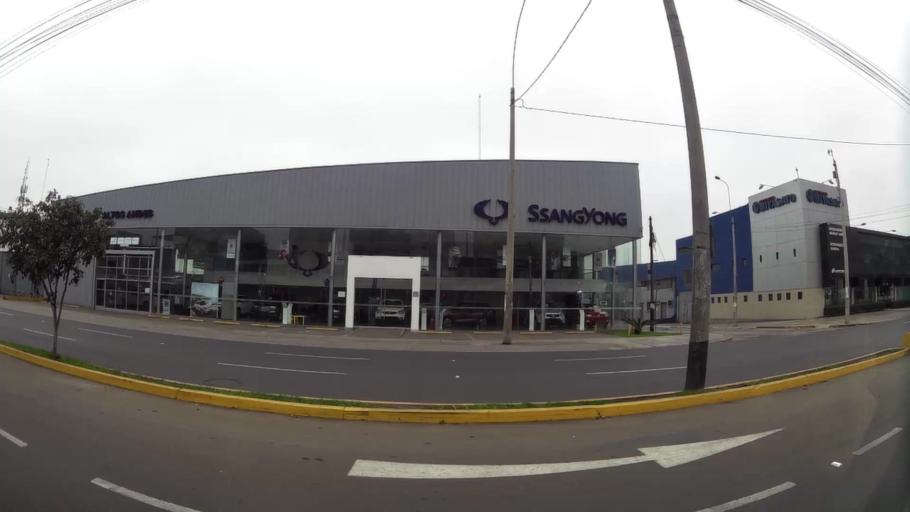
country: PE
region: Lima
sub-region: Lima
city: Surco
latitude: -12.1075
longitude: -77.0159
